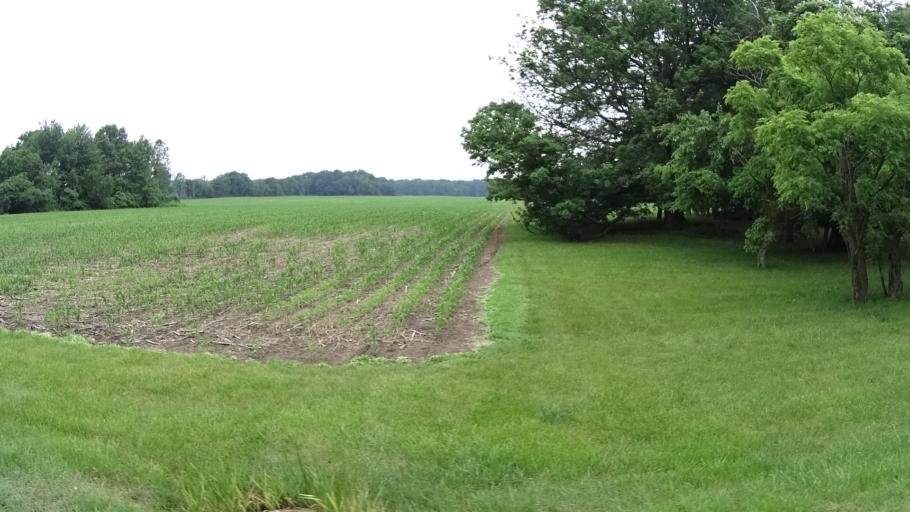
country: US
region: Ohio
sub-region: Erie County
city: Milan
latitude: 41.2996
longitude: -82.5603
